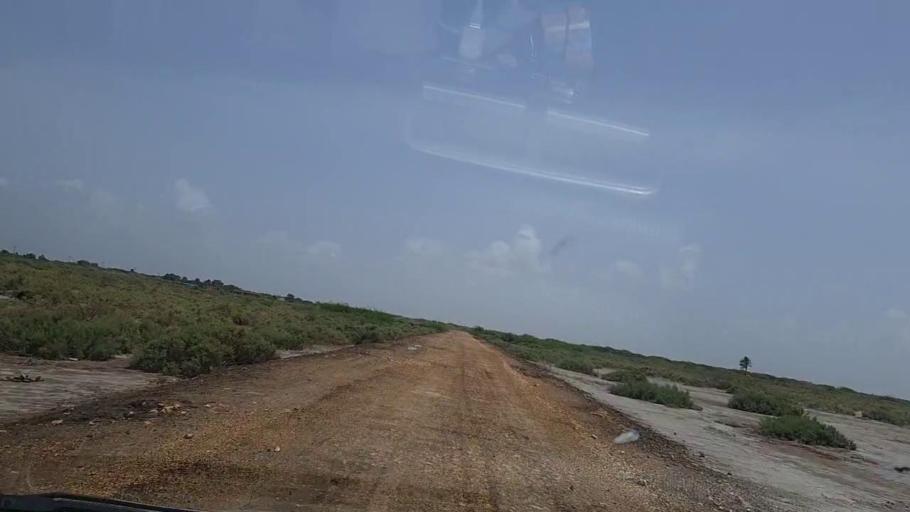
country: PK
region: Sindh
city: Keti Bandar
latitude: 24.1554
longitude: 67.5291
